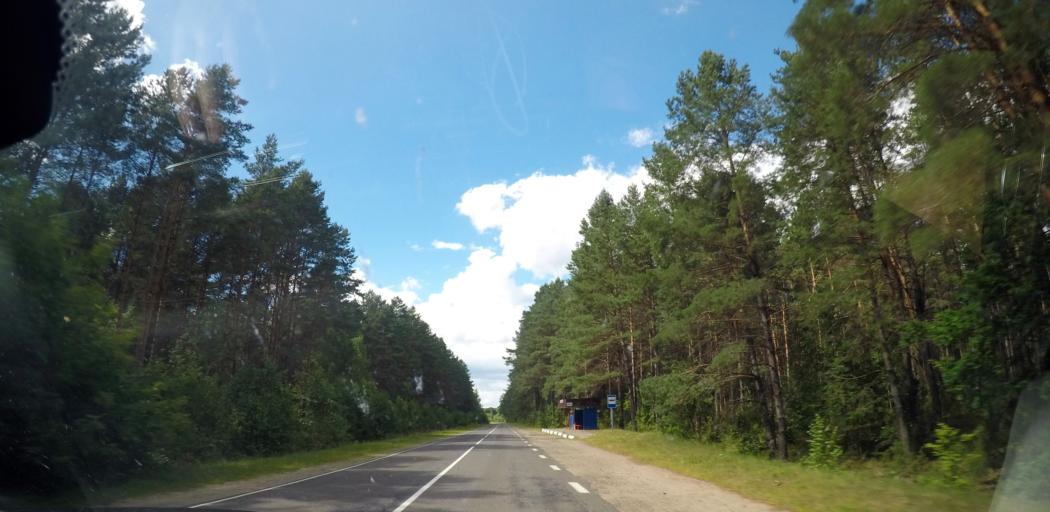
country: LT
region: Alytaus apskritis
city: Druskininkai
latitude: 53.8673
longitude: 24.1669
